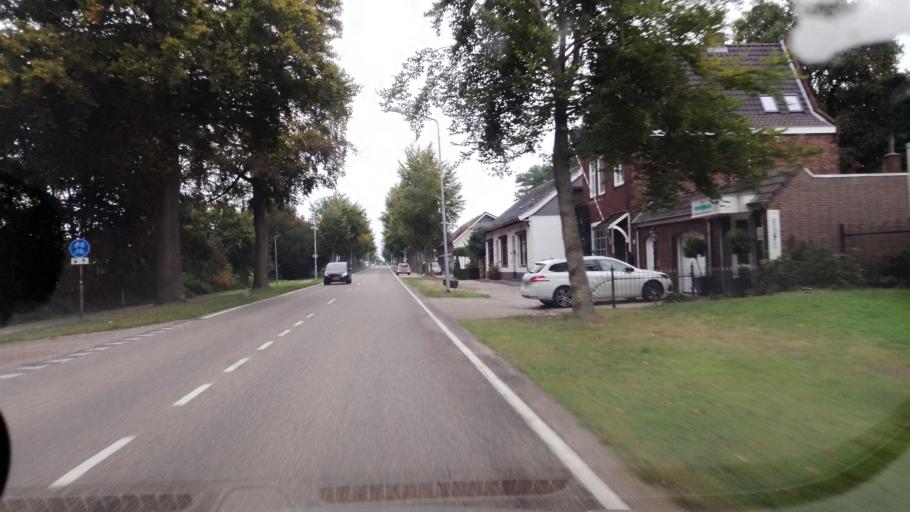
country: NL
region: Limburg
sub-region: Gemeente Venlo
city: Tegelen
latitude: 51.3550
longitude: 6.1268
